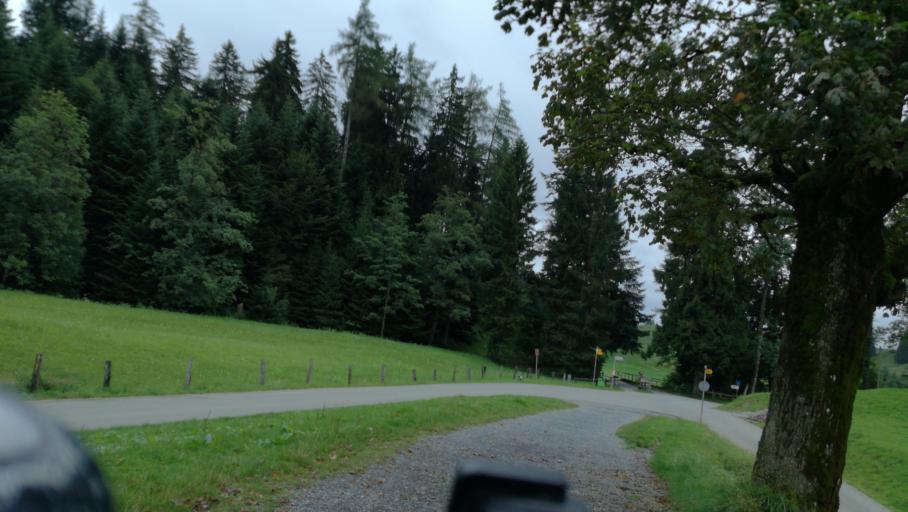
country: CH
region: Zug
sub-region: Zug
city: Zug
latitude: 47.1383
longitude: 8.5330
